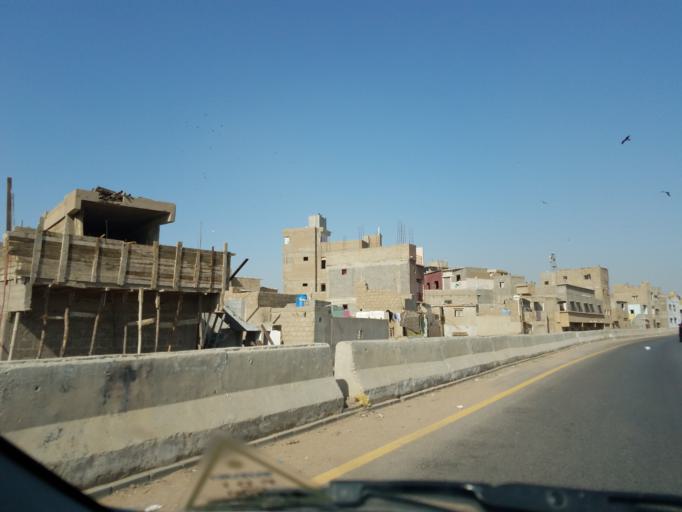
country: PK
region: Sindh
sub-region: Karachi District
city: Karachi
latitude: 24.8894
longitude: 67.0263
